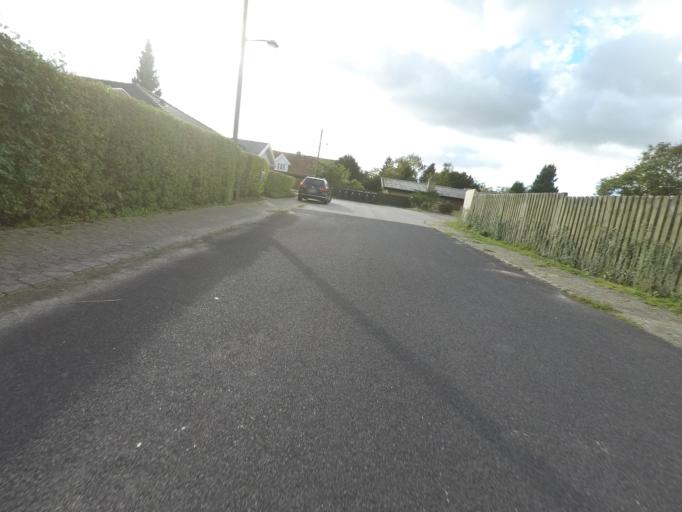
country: DK
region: Capital Region
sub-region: Ballerup Kommune
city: Ballerup
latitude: 55.7500
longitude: 12.3895
